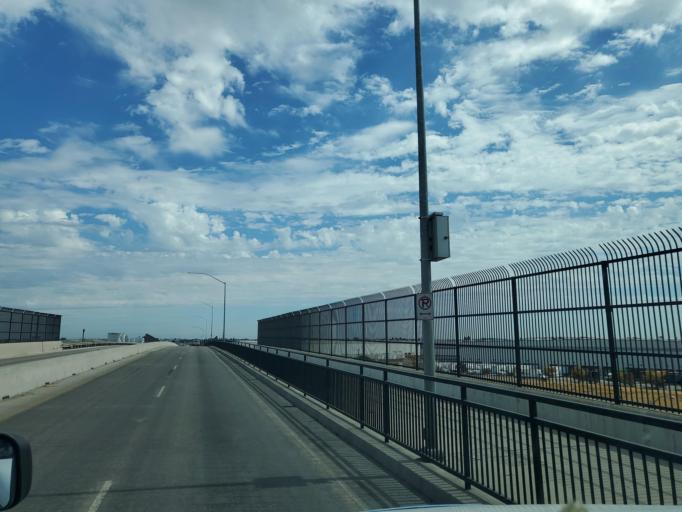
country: US
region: California
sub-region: San Joaquin County
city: French Camp
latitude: 37.8975
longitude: -121.2700
